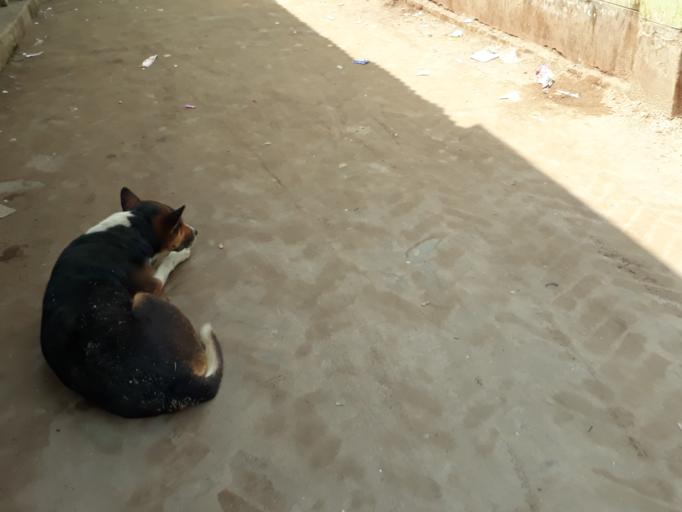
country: BD
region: Dhaka
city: Tungi
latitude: 23.9211
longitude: 90.4015
